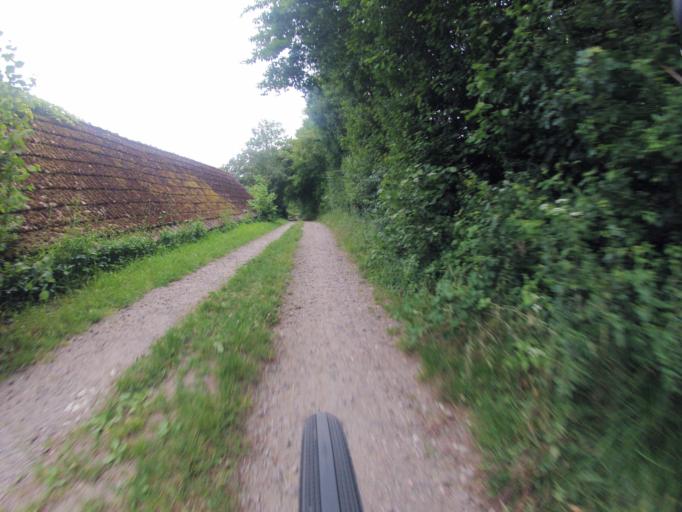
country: DE
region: North Rhine-Westphalia
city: Ibbenburen
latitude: 52.2293
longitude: 7.7237
